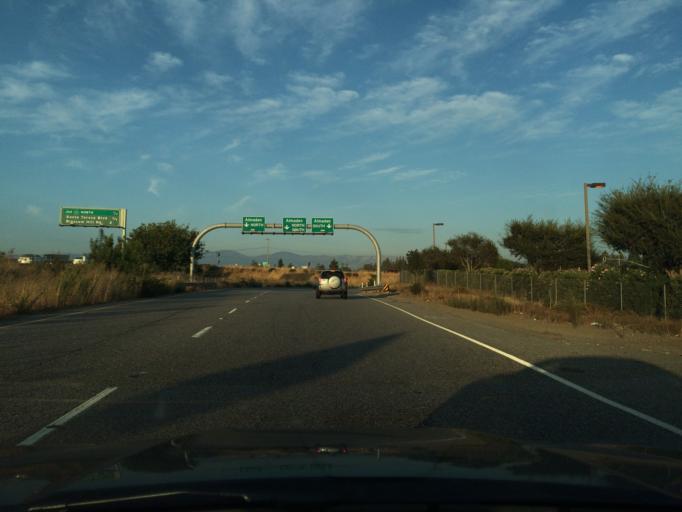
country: US
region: California
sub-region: Santa Clara County
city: Seven Trees
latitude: 37.2544
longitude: -121.8787
